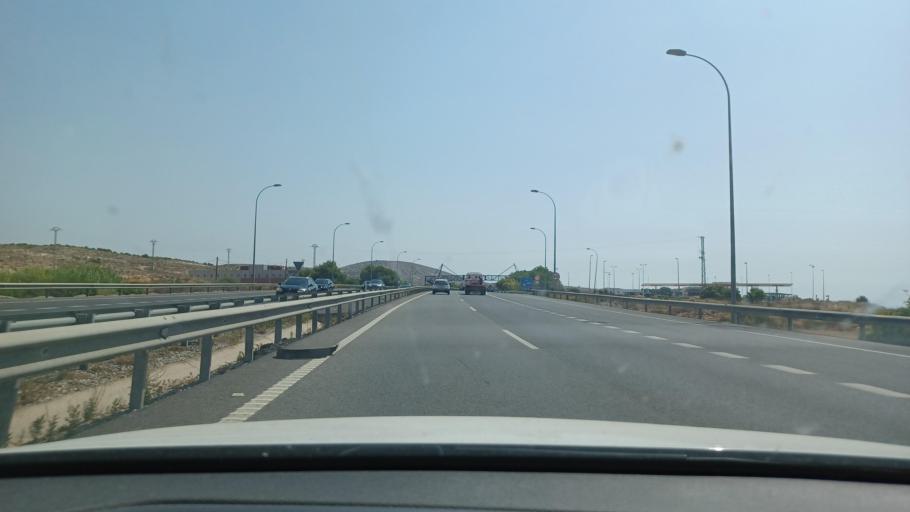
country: ES
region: Valencia
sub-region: Provincia de Alicante
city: Elche
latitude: 38.3080
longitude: -0.6094
